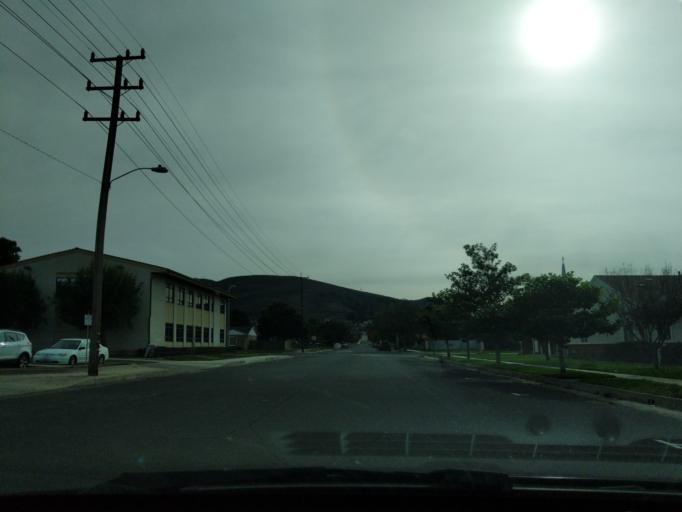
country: US
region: California
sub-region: Santa Barbara County
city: Lompoc
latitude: 34.6380
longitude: -120.4541
